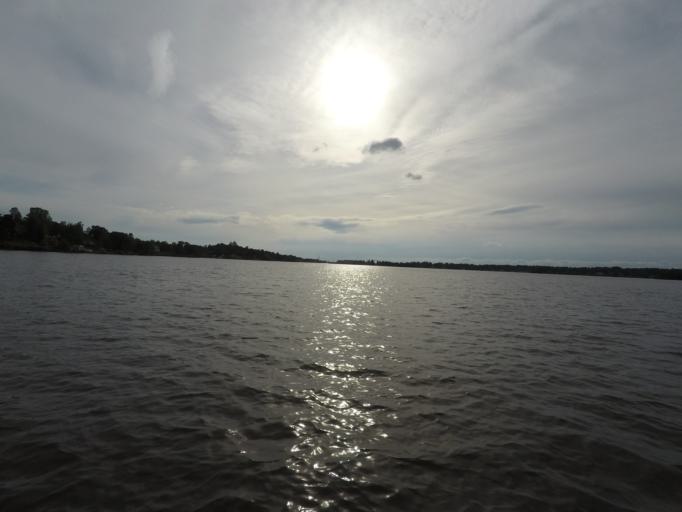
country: SE
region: Soedermanland
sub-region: Eskilstuna Kommun
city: Kvicksund
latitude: 59.4543
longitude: 16.3455
